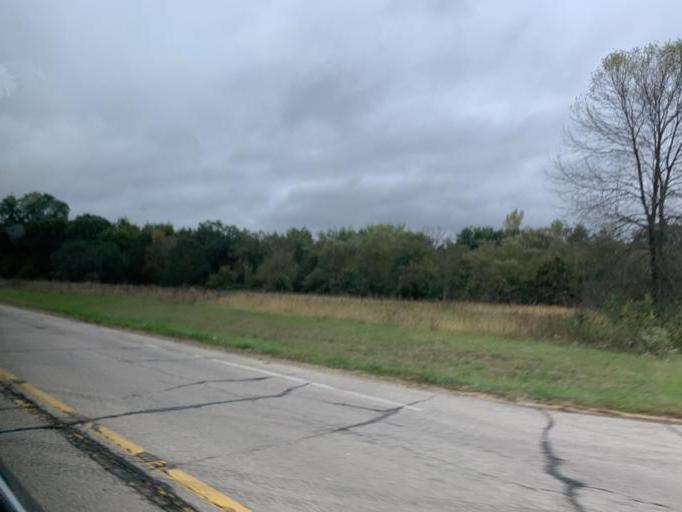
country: US
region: Wisconsin
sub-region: Grant County
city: Muscoda
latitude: 43.2060
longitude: -90.4513
